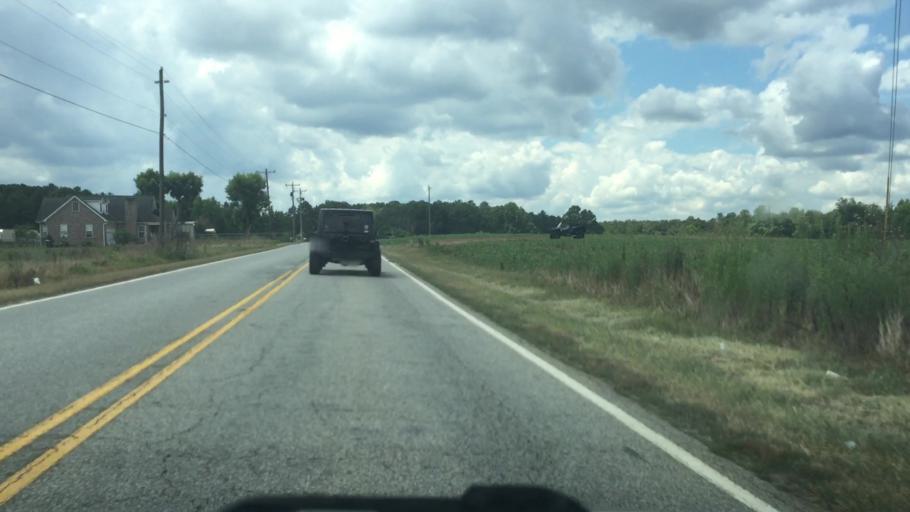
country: US
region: North Carolina
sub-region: Rowan County
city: Enochville
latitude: 35.5851
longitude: -80.6532
